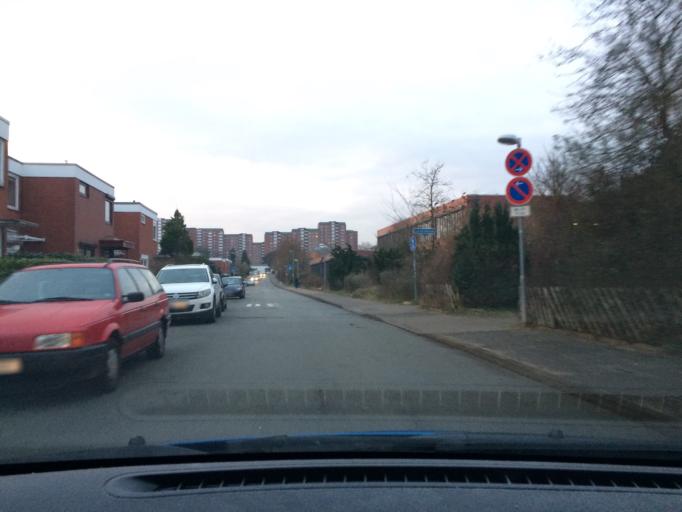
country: DE
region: Lower Saxony
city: Lueneburg
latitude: 53.2389
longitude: 10.4405
